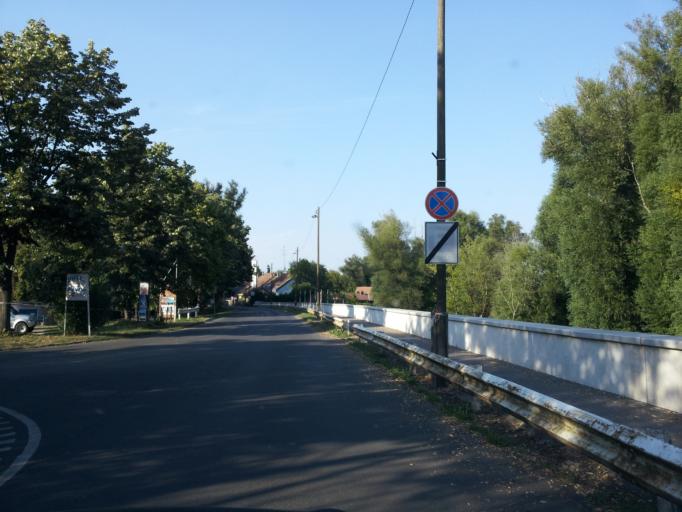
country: HU
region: Pest
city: Szentendre
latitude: 47.6715
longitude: 19.0796
